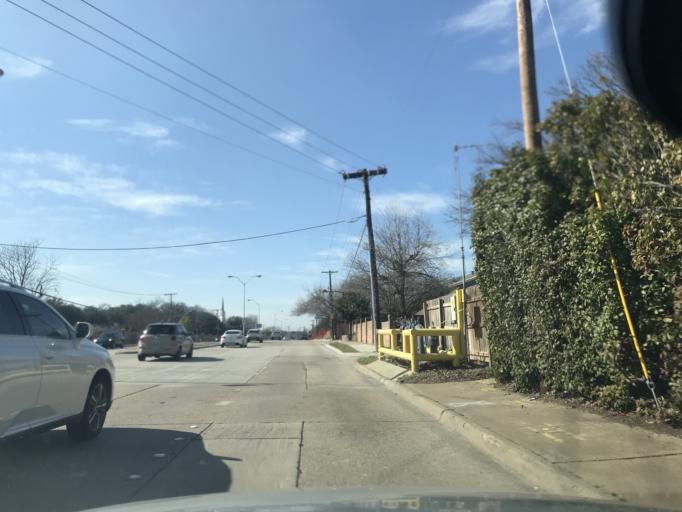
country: US
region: Texas
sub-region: Collin County
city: Plano
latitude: 33.0412
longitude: -96.7644
